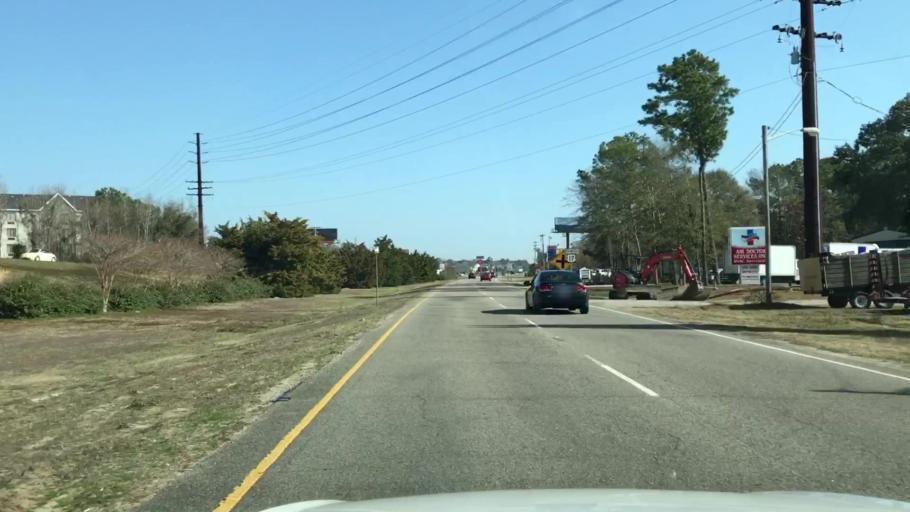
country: US
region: South Carolina
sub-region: Georgetown County
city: Murrells Inlet
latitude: 33.5742
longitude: -79.0282
